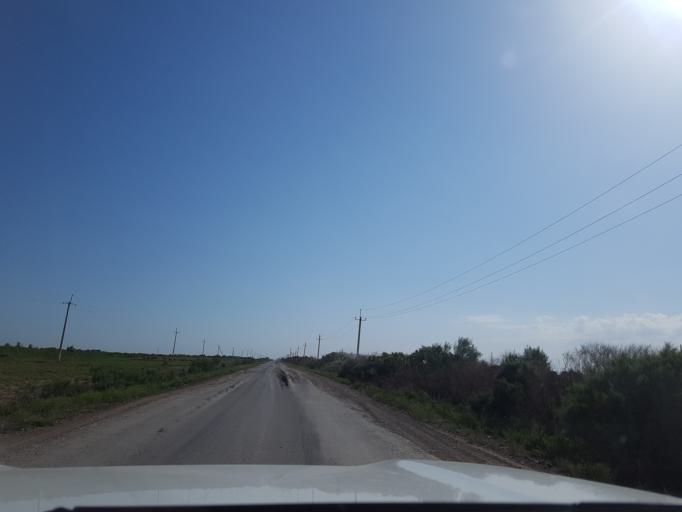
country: TM
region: Dasoguz
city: Koeneuergench
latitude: 42.0842
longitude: 58.8789
